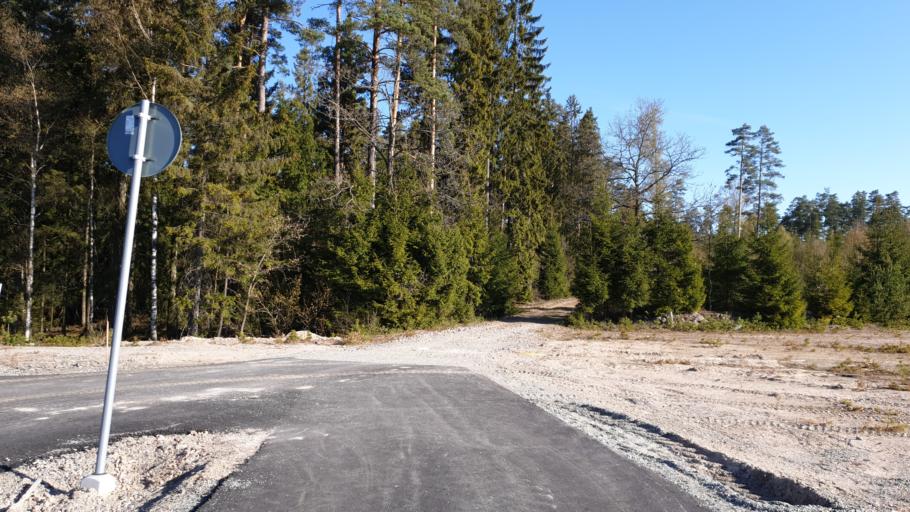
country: SE
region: Kronoberg
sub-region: Ljungby Kommun
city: Ljungby
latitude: 56.8301
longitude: 13.9016
